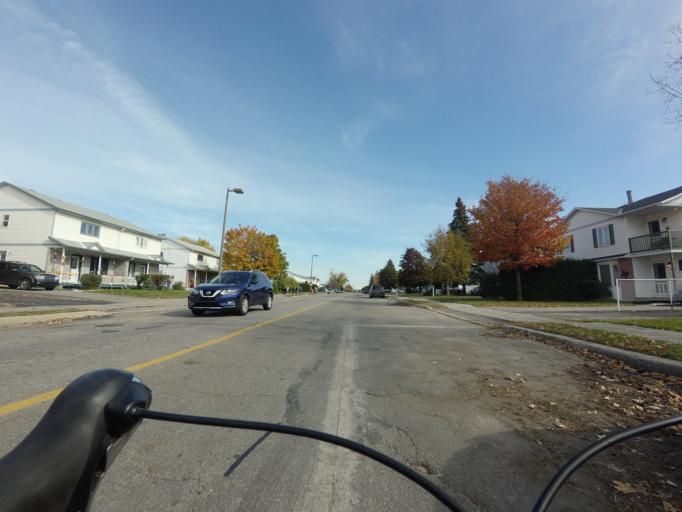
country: CA
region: Quebec
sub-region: Outaouais
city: Gatineau
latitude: 45.5073
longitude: -75.6548
